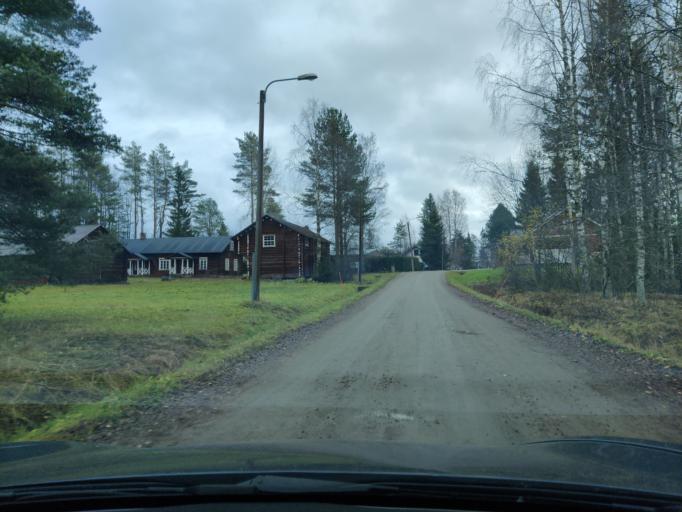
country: FI
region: Northern Savo
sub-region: Ylae-Savo
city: Kiuruvesi
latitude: 63.6491
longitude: 26.6296
